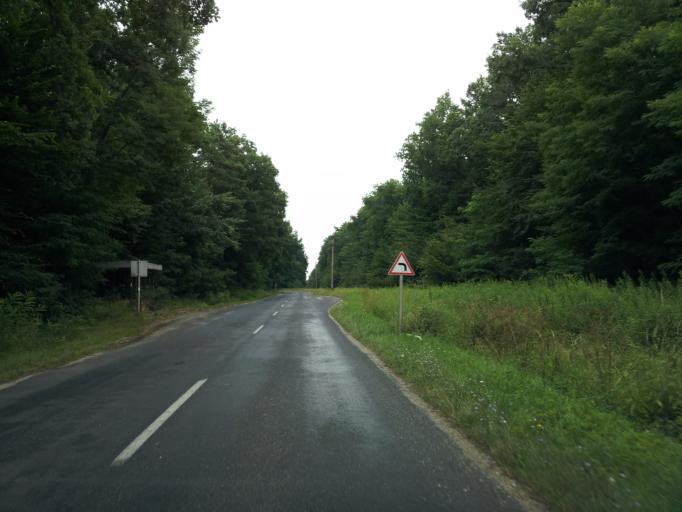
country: HU
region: Zala
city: Turje
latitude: 47.0540
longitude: 17.0138
